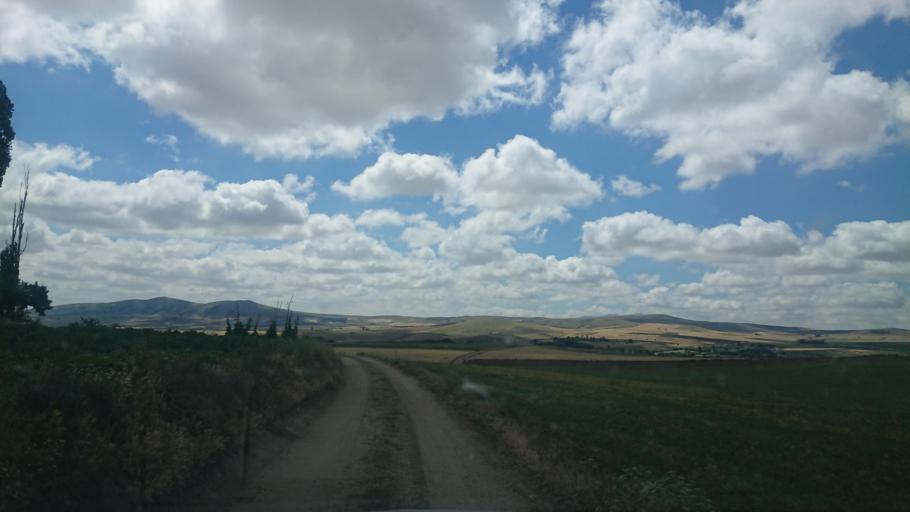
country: TR
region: Aksaray
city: Agacoren
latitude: 38.8317
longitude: 33.9509
